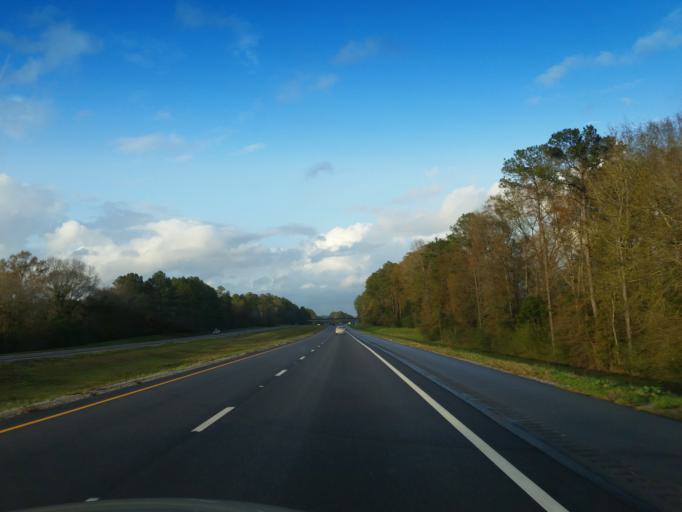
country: US
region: Mississippi
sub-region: Jones County
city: Sharon
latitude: 31.8295
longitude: -89.0504
